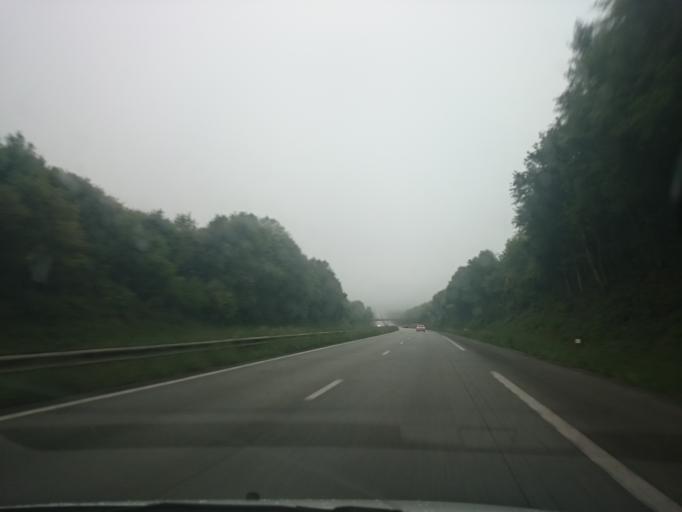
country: FR
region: Brittany
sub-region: Departement du Finistere
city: Briec
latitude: 48.1292
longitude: -4.0234
